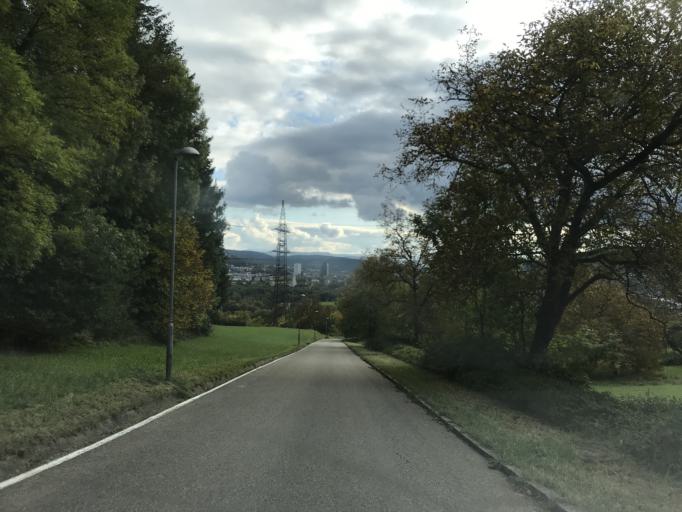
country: DE
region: Baden-Wuerttemberg
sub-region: Freiburg Region
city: Loerrach
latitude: 47.6361
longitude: 7.6669
